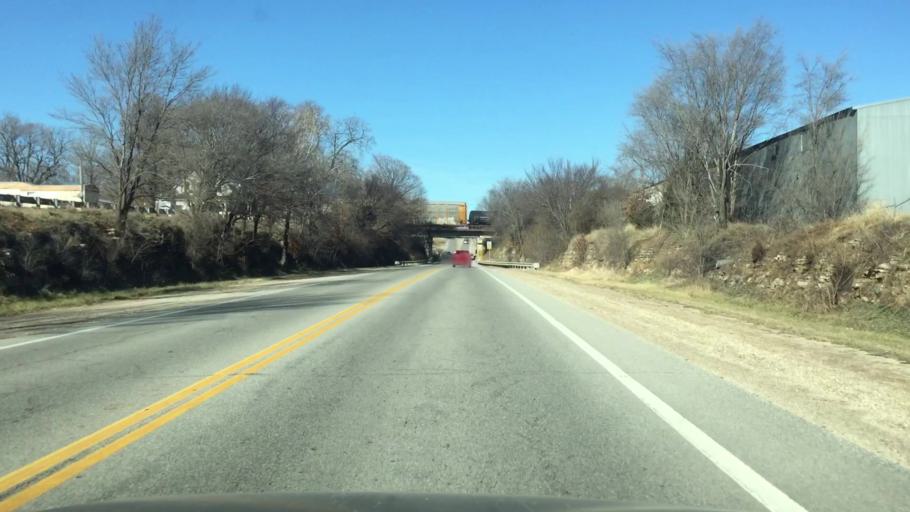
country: US
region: Kansas
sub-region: Anderson County
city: Garnett
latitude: 38.2723
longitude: -95.2492
